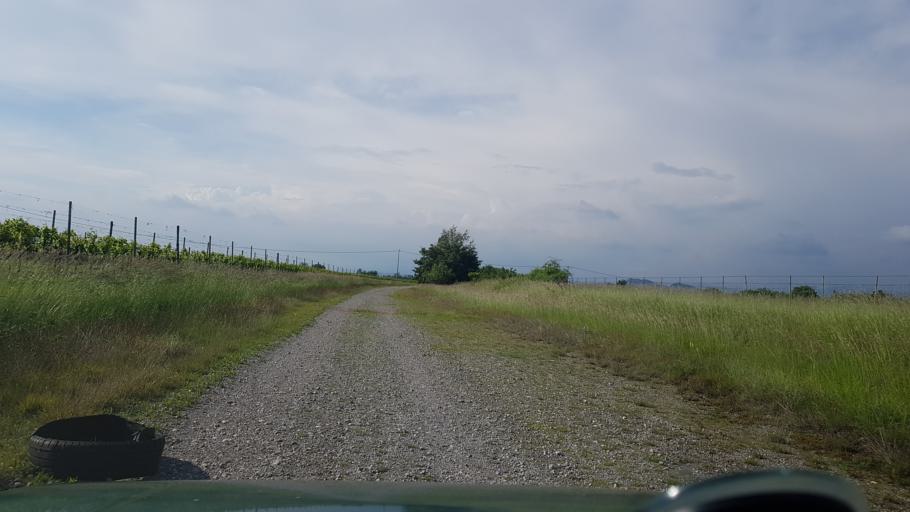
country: IT
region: Friuli Venezia Giulia
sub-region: Provincia di Gorizia
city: Mariano del Friuli
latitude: 45.8947
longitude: 13.4666
